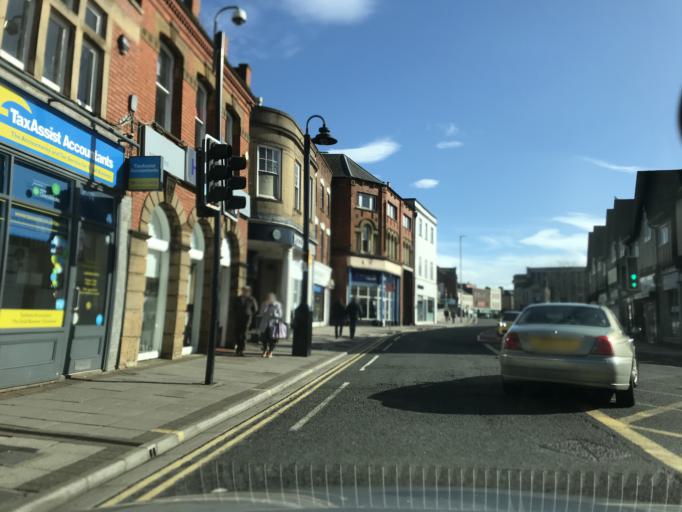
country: GB
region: England
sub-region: Somerset
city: Taunton
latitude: 51.0183
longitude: -3.1047
